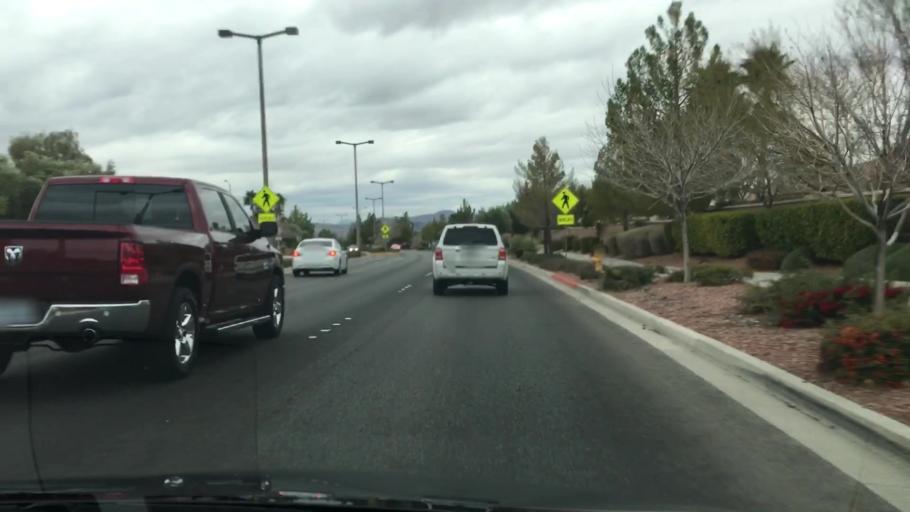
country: US
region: Nevada
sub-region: Clark County
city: Whitney
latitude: 35.9468
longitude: -115.0969
